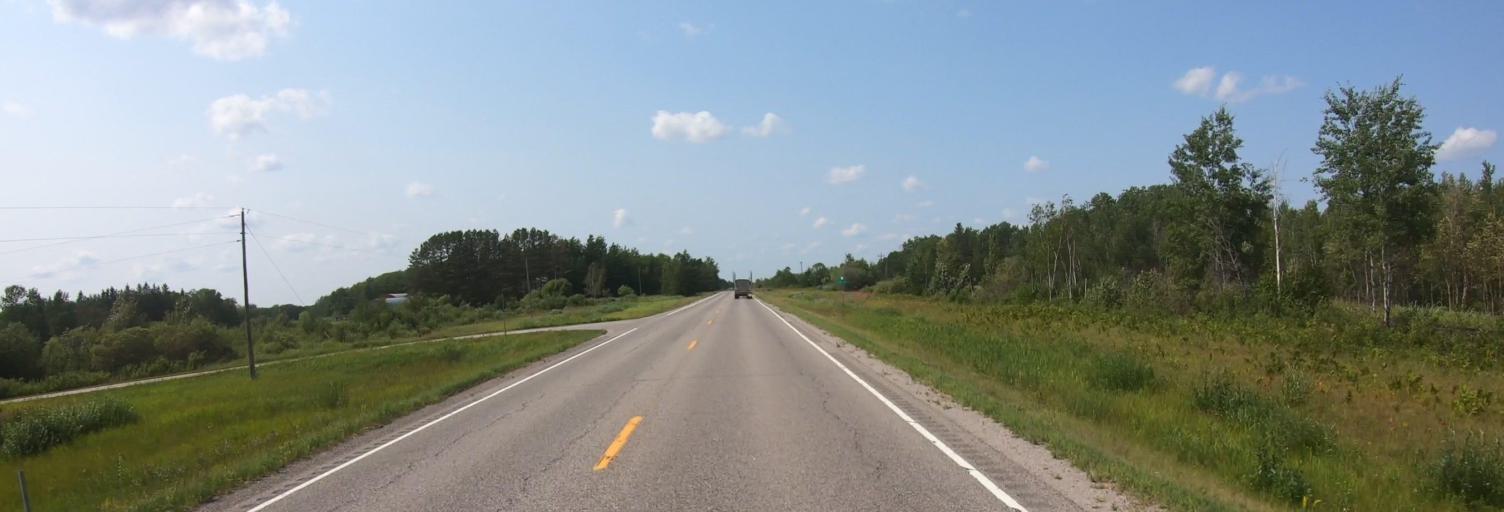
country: US
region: Minnesota
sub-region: Roseau County
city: Warroad
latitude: 48.8171
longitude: -95.1334
